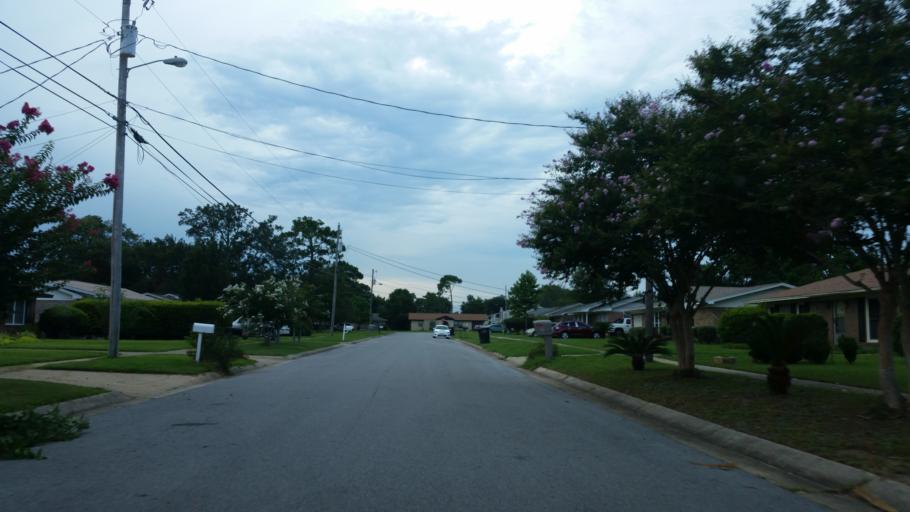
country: US
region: Florida
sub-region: Escambia County
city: Ferry Pass
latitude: 30.5072
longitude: -87.1818
